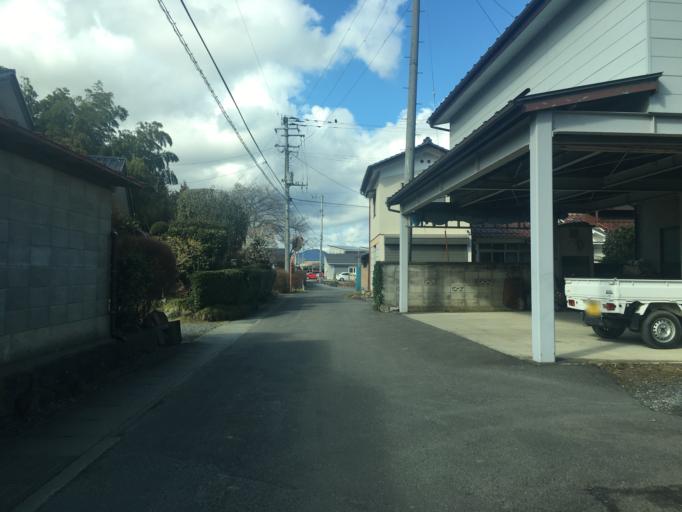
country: JP
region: Fukushima
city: Fukushima-shi
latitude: 37.7505
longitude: 140.4300
